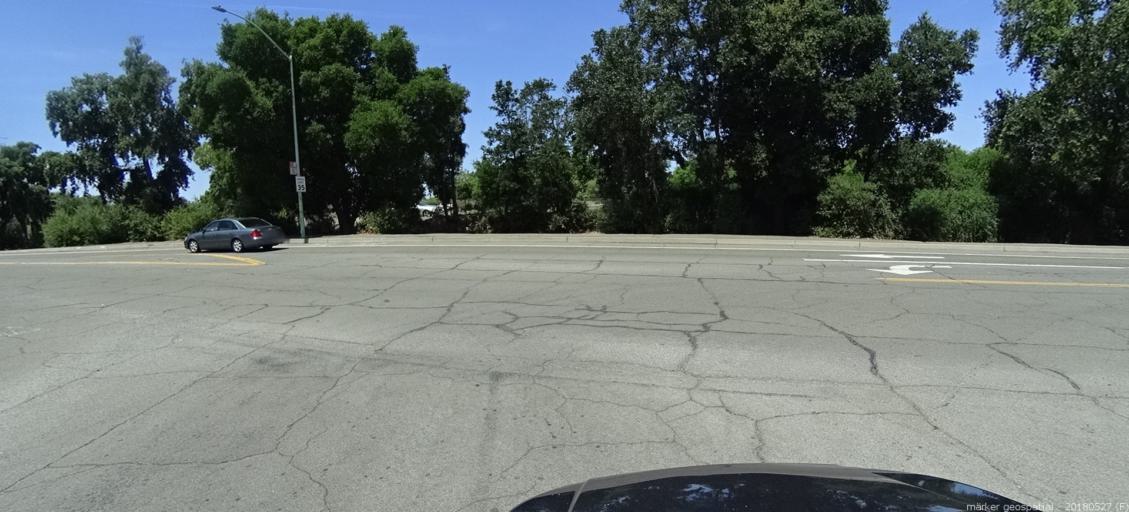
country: US
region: California
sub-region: Sacramento County
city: Sacramento
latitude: 38.5398
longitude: -121.5105
